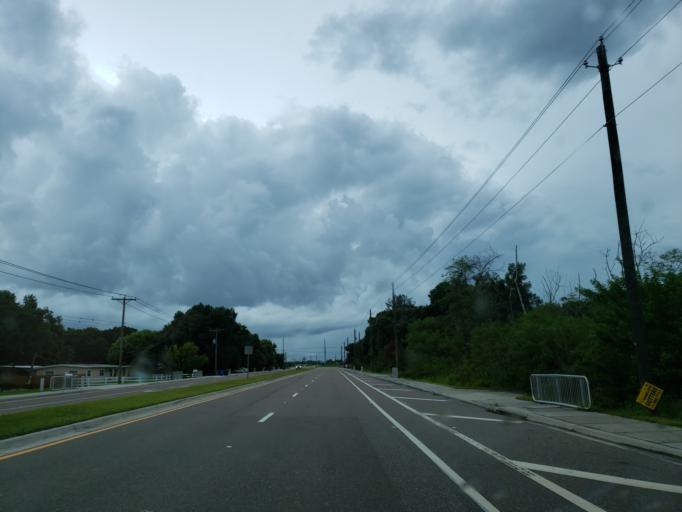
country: US
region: Florida
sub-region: Hillsborough County
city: Ruskin
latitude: 27.7140
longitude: -82.4021
